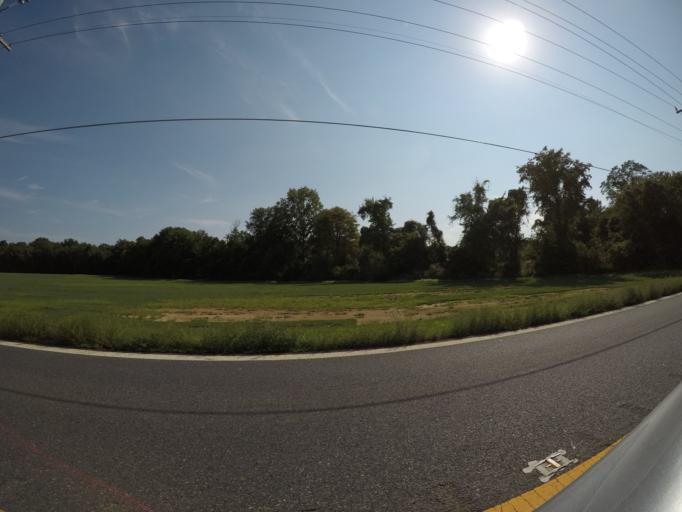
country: US
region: Maryland
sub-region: Harford County
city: Aberdeen
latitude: 39.5640
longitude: -76.2071
